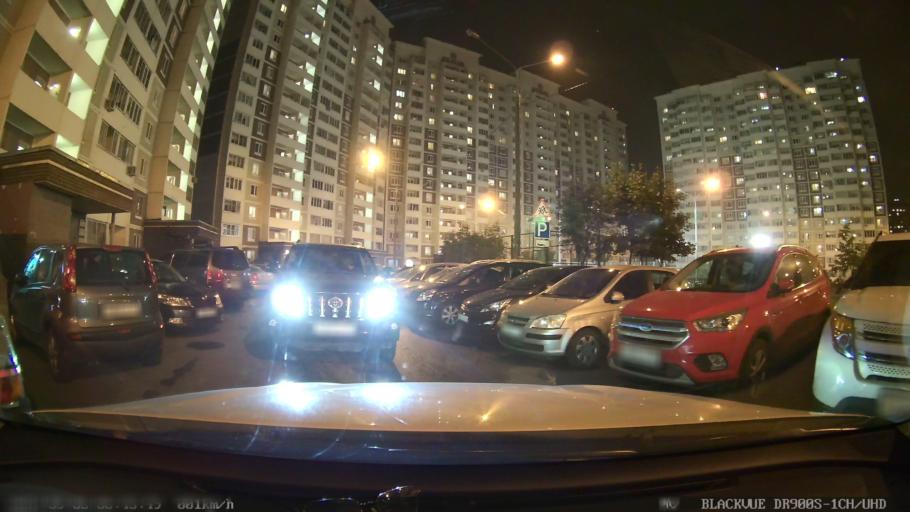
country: RU
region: Moskovskaya
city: Lobnya
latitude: 56.0045
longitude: 37.4472
